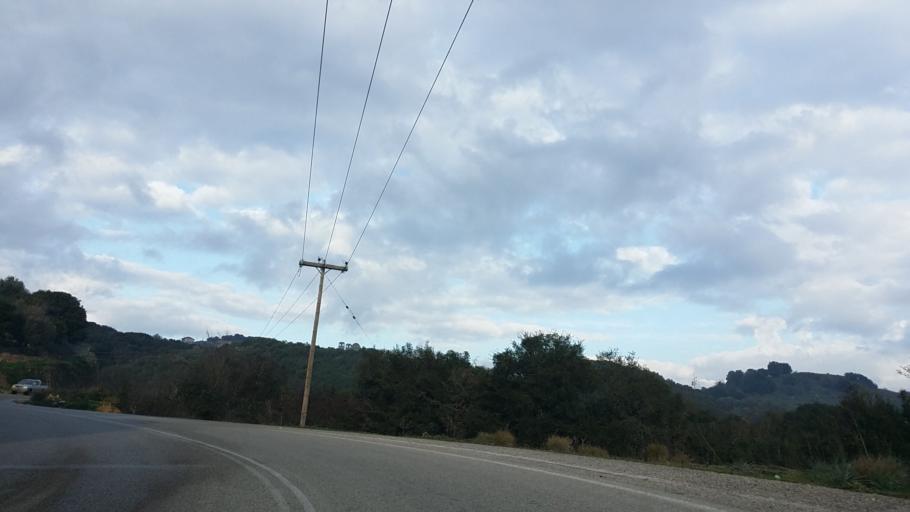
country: GR
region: West Greece
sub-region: Nomos Aitolias kai Akarnanias
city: Katouna
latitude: 38.7799
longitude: 21.1246
